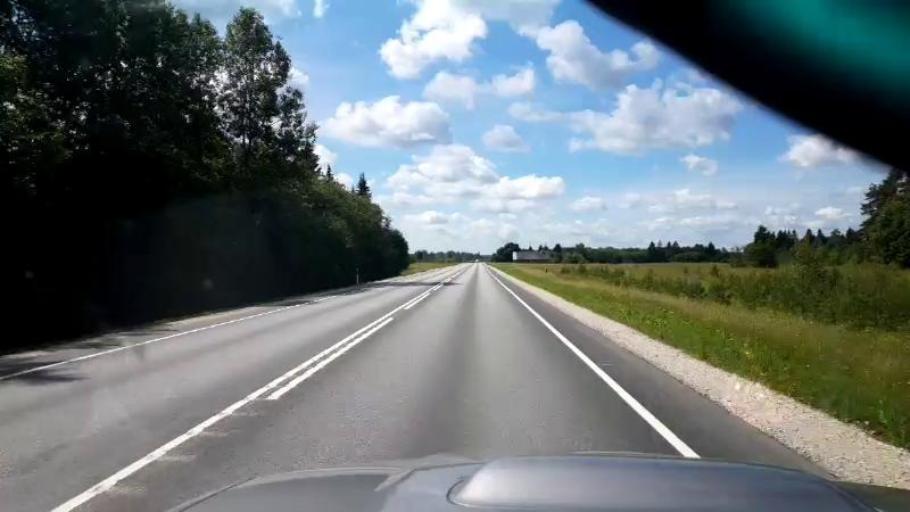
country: EE
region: Laeaene-Virumaa
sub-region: Tapa vald
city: Tapa
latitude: 59.2741
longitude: 26.0382
